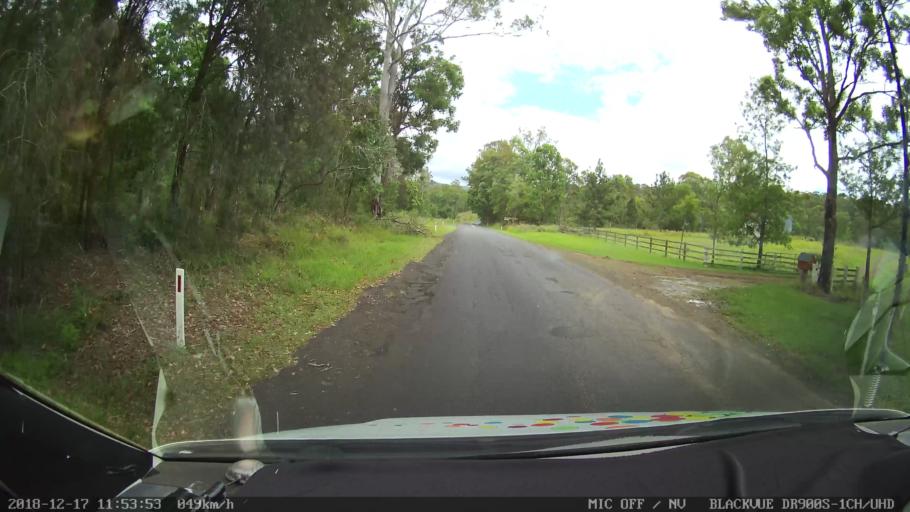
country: AU
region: New South Wales
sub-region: Kyogle
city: Kyogle
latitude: -28.5712
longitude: 152.5855
